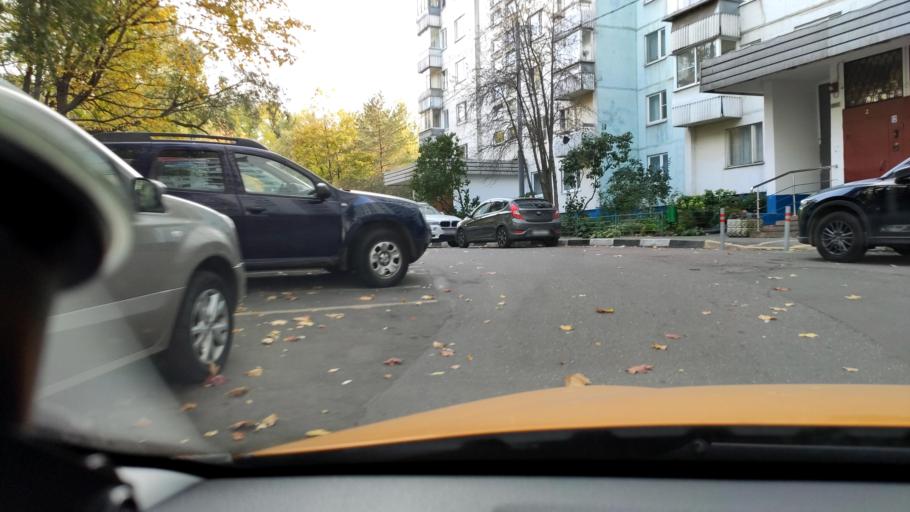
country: RU
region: Moscow
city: Yasenevo
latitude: 55.5966
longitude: 37.5401
